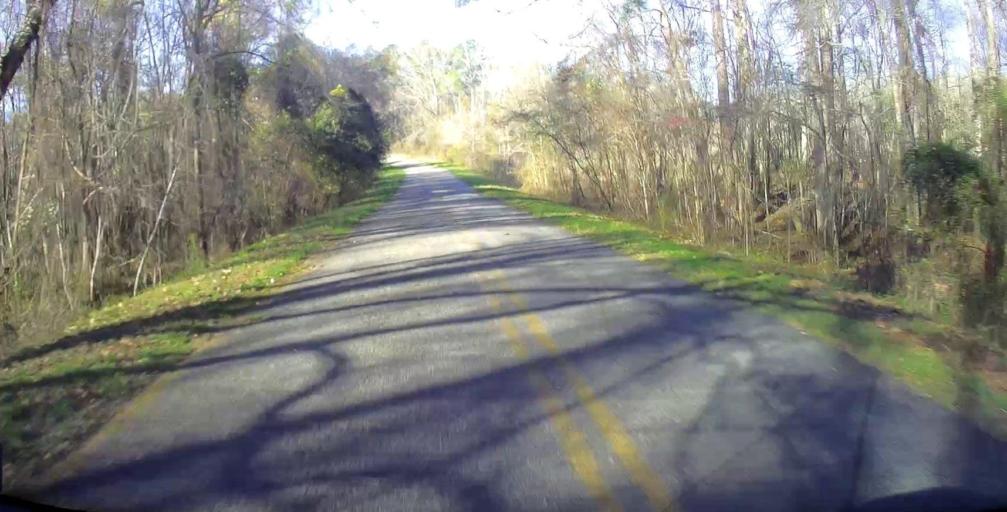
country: US
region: Georgia
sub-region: Macon County
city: Marshallville
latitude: 32.4739
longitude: -83.9515
